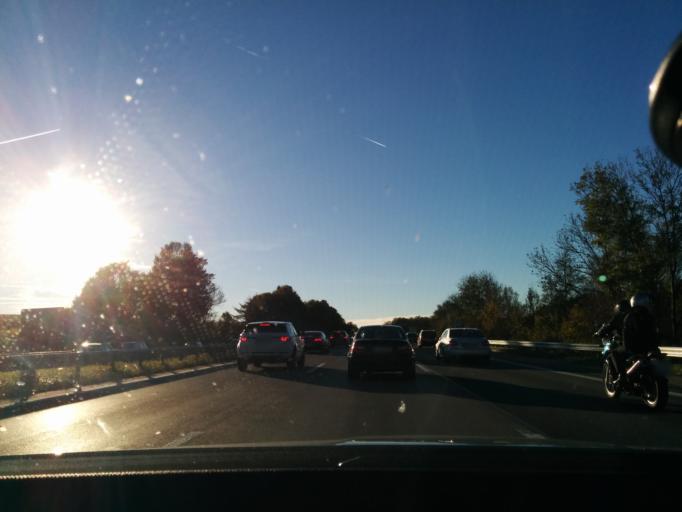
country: DE
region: Bavaria
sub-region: Upper Bavaria
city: Weyarn
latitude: 47.8648
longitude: 11.8057
